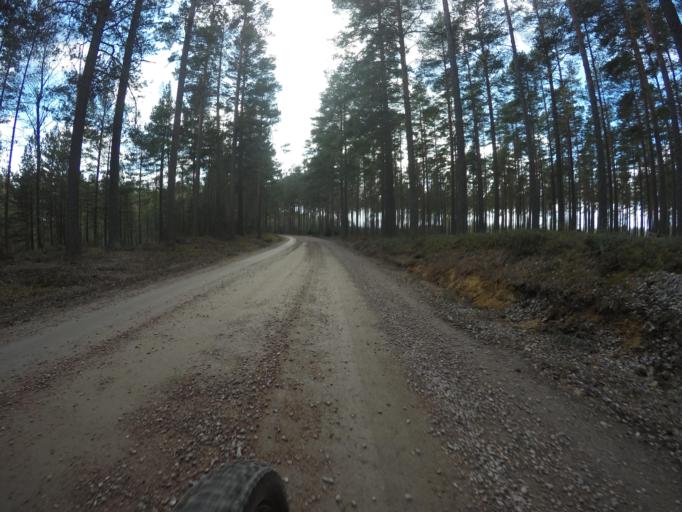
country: SE
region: Vaestmanland
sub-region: Kungsors Kommun
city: Kungsoer
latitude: 59.3729
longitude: 16.1014
